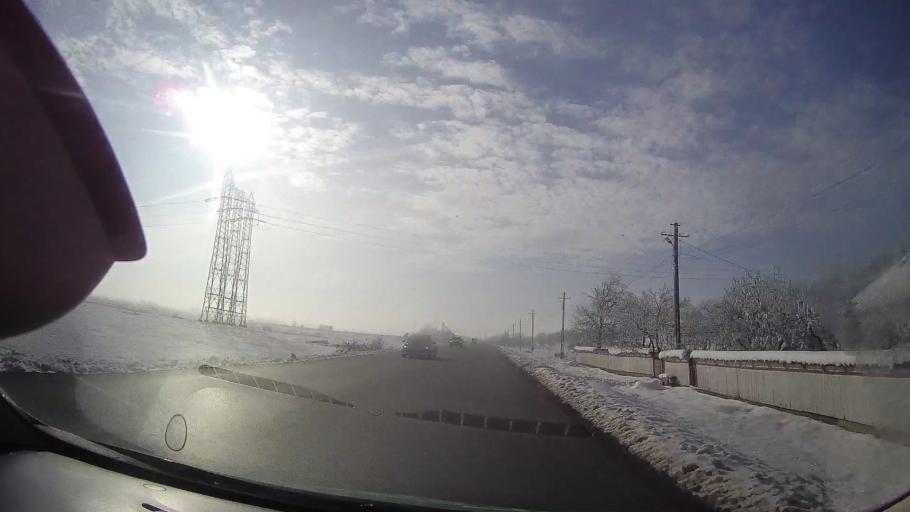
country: RO
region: Iasi
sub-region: Comuna Cristesti
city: Cristesti
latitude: 47.2544
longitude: 26.5535
